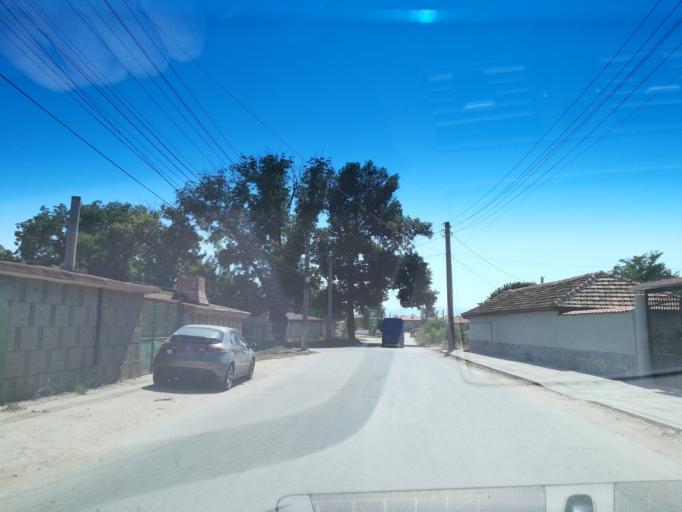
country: BG
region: Pazardzhik
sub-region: Obshtina Pazardzhik
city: Pazardzhik
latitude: 42.2732
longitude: 24.3968
